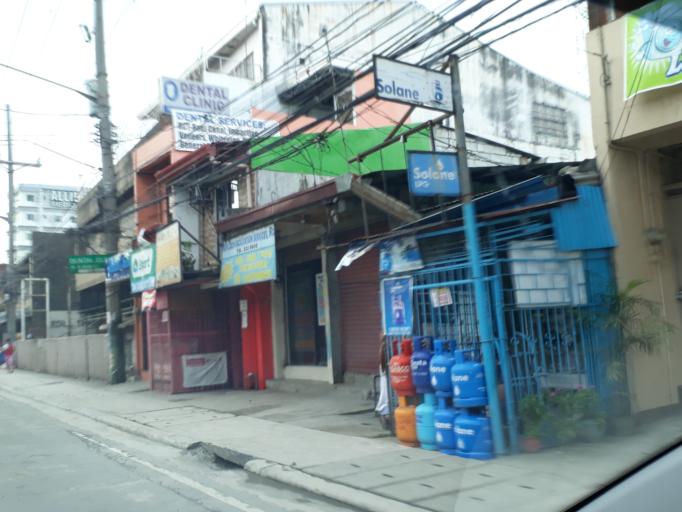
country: PH
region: Calabarzon
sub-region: Province of Rizal
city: Valenzuela
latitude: 14.7168
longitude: 120.9574
